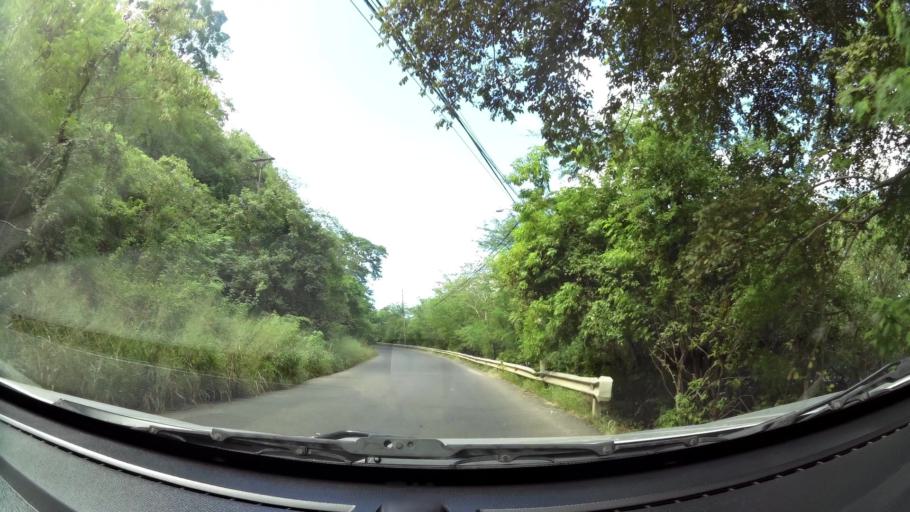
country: CR
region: Guanacaste
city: Santa Cruz
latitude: 10.3093
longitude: -85.8337
